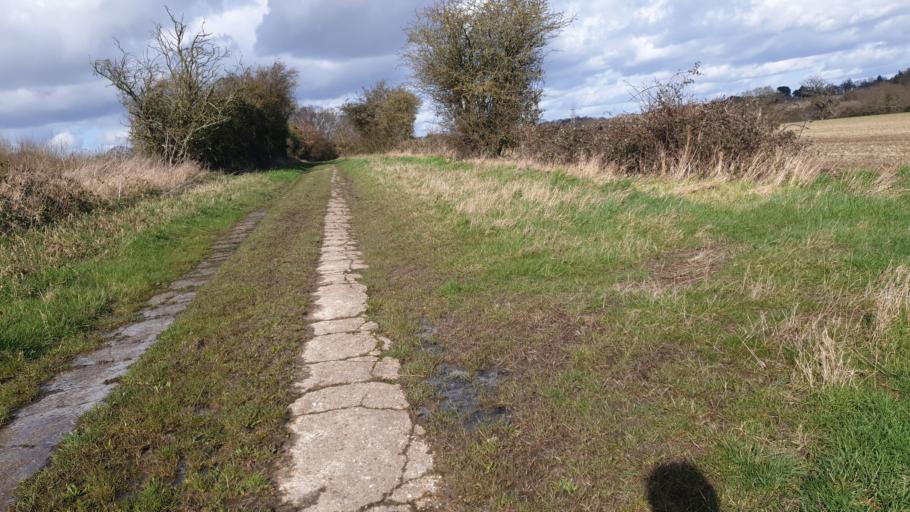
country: GB
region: England
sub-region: Essex
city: Little Clacton
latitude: 51.8427
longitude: 1.1636
